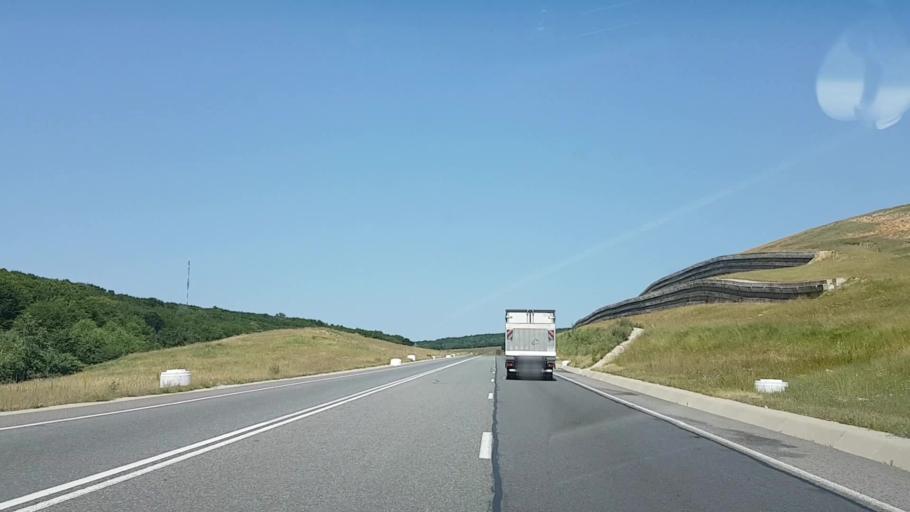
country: RO
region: Cluj
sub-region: Comuna Feleacu
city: Feleacu
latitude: 46.6968
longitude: 23.6367
